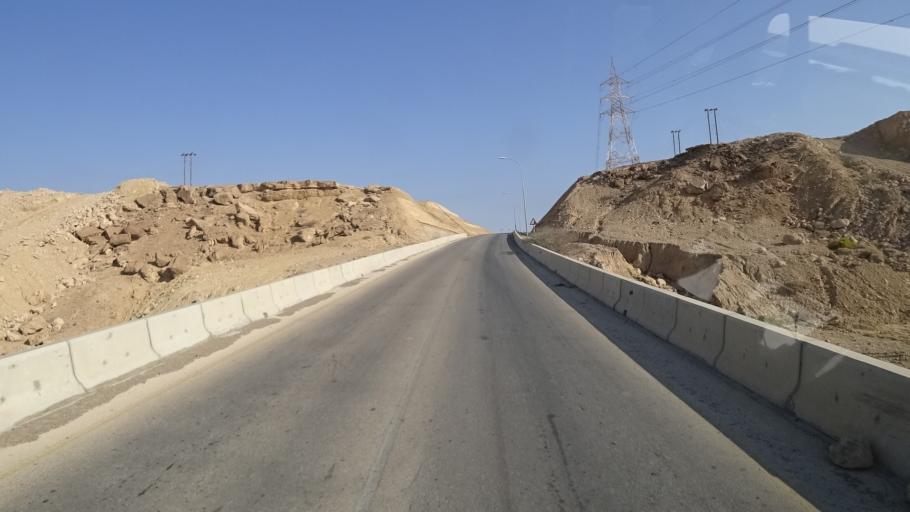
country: OM
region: Ash Sharqiyah
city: Sur
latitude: 22.5850
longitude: 59.4563
